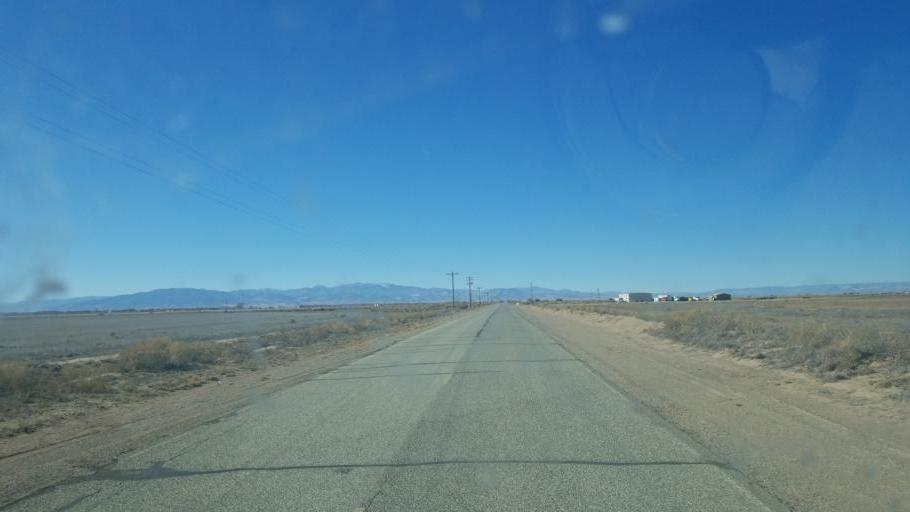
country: US
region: Colorado
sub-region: Alamosa County
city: Alamosa
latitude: 37.5746
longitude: -105.9142
